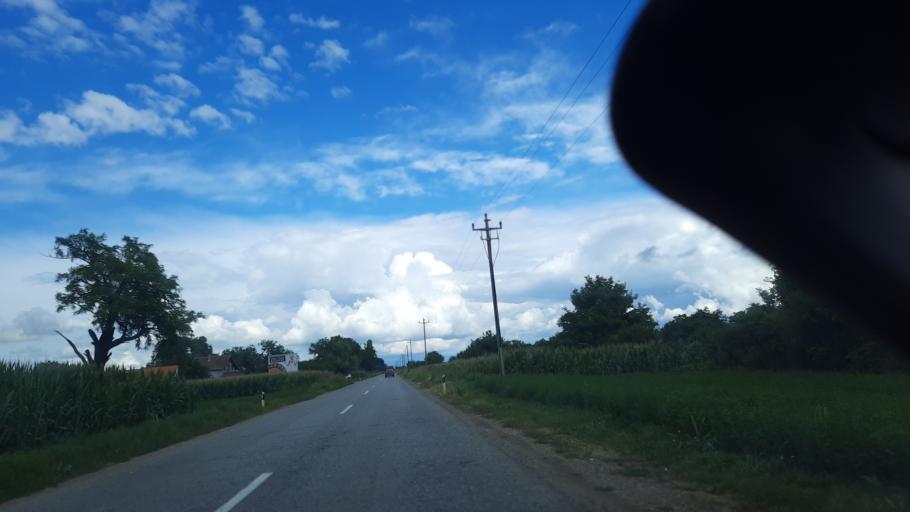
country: RS
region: Autonomna Pokrajina Vojvodina
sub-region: Sremski Okrug
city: Sremska Mitrovica
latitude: 44.9755
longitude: 19.6628
